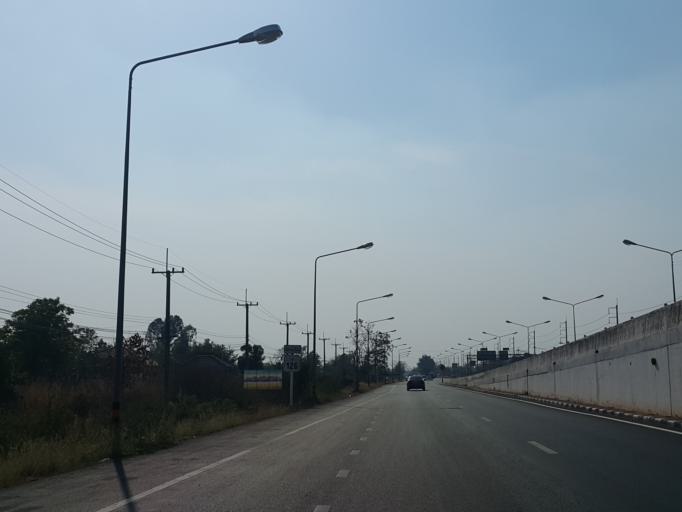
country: TH
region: Phitsanulok
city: Phitsanulok
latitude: 16.8475
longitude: 100.3433
